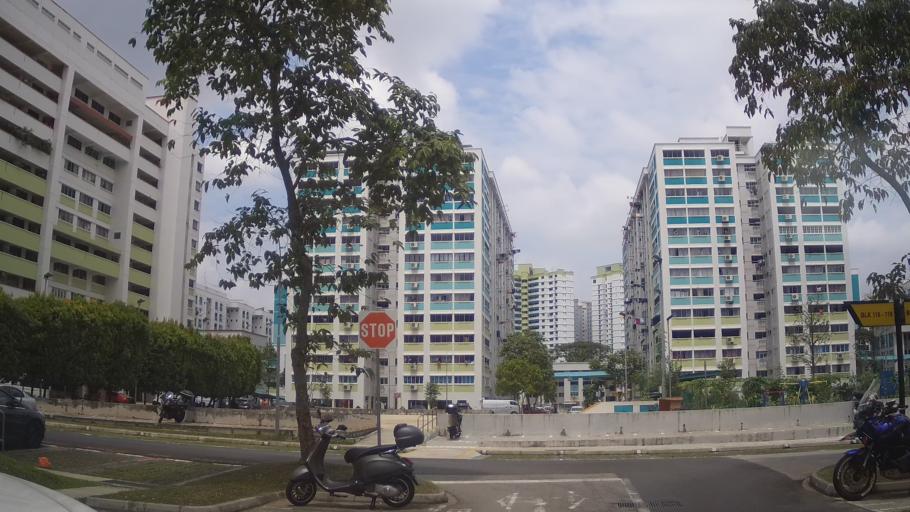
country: MY
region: Johor
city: Johor Bahru
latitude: 1.3772
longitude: 103.7693
